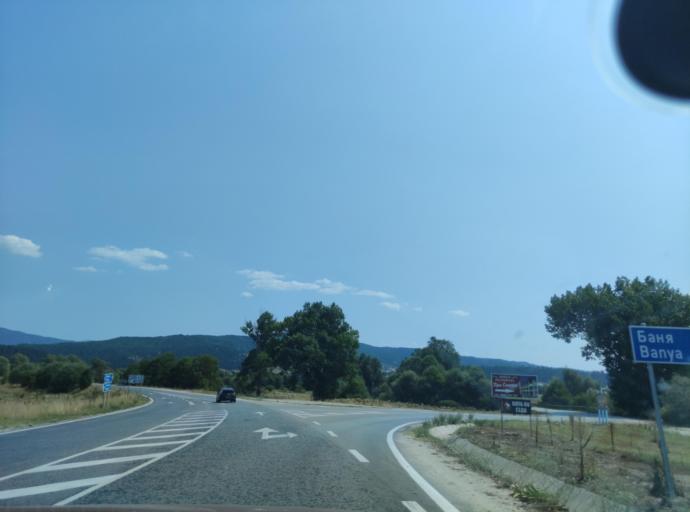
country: BG
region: Blagoevgrad
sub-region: Obshtina Razlog
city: Razlog
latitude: 41.8865
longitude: 23.5076
